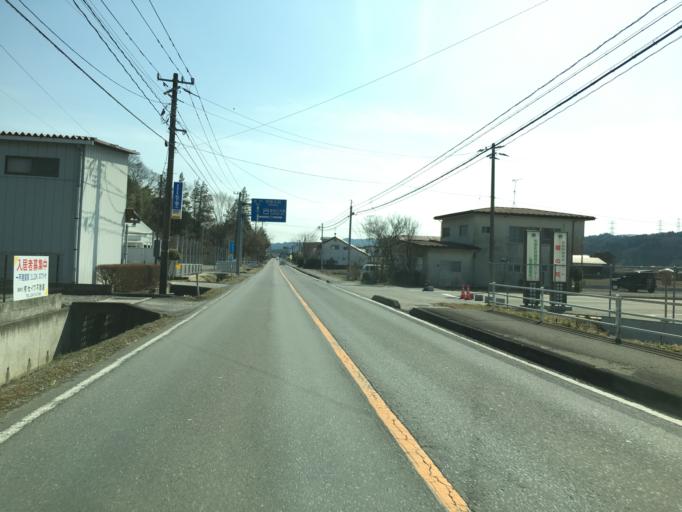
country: JP
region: Ibaraki
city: Daigo
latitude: 36.9067
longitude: 140.4178
